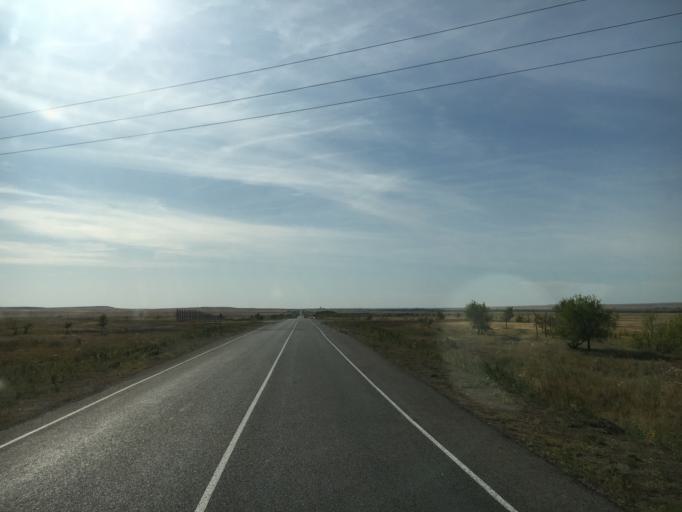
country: KZ
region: Batys Qazaqstan
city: Kamenka
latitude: 51.1084
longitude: 50.4395
